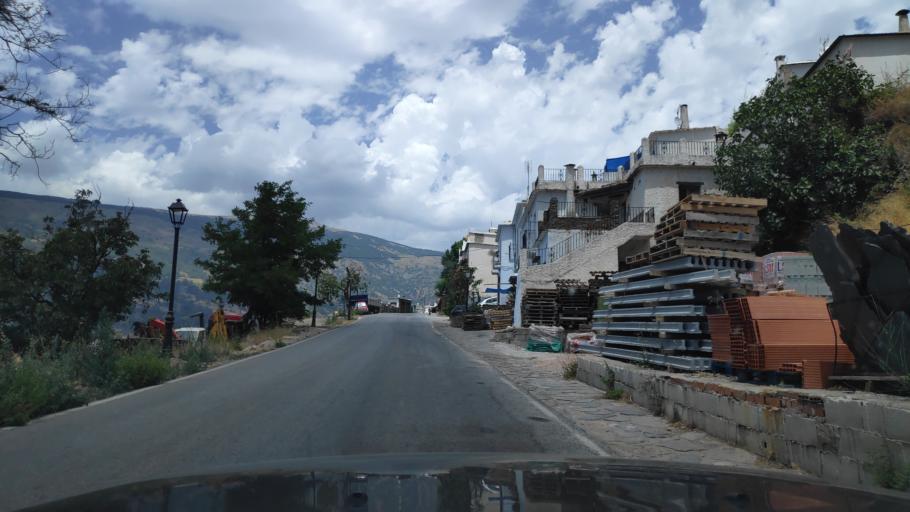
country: ES
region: Andalusia
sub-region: Provincia de Granada
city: Bubion
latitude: 36.9460
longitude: -3.3540
